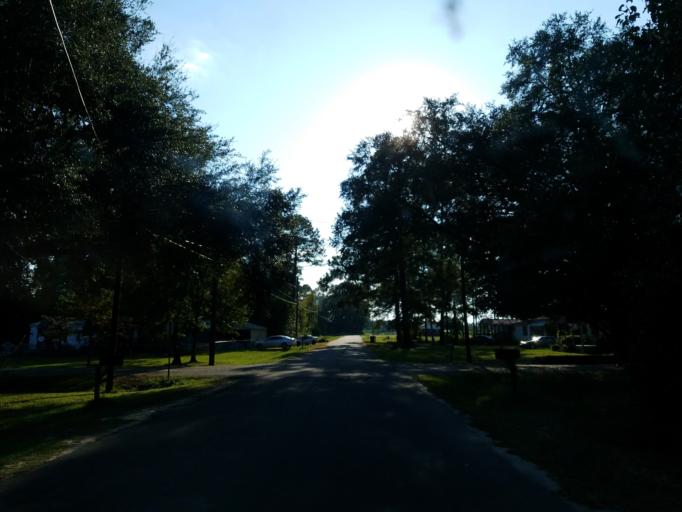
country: US
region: Georgia
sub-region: Cook County
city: Sparks
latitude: 31.2695
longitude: -83.4666
